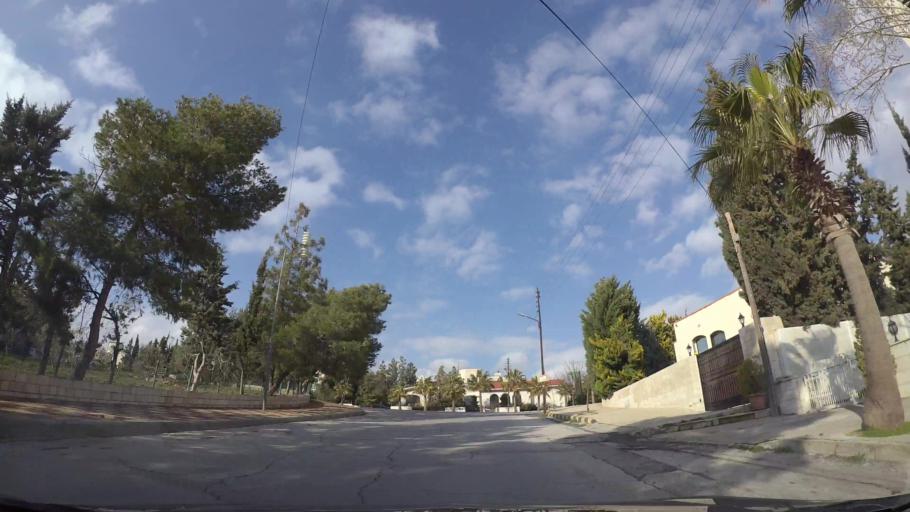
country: JO
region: Amman
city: Al Jubayhah
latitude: 31.9823
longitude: 35.8800
